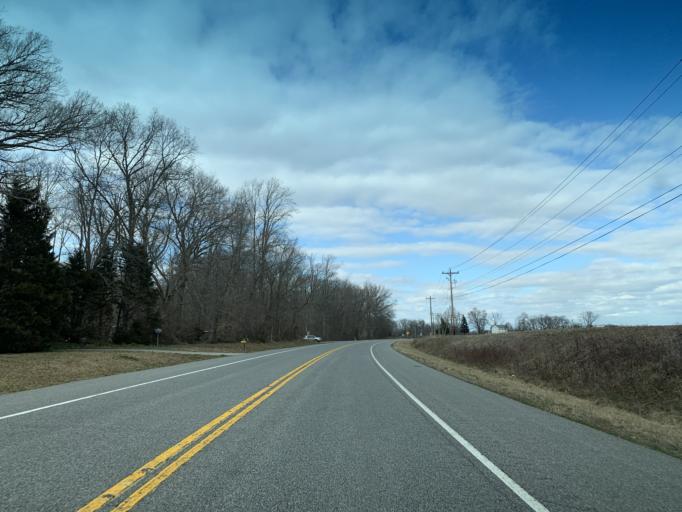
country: US
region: Maryland
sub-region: Queen Anne's County
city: Centreville
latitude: 38.9947
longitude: -76.0752
